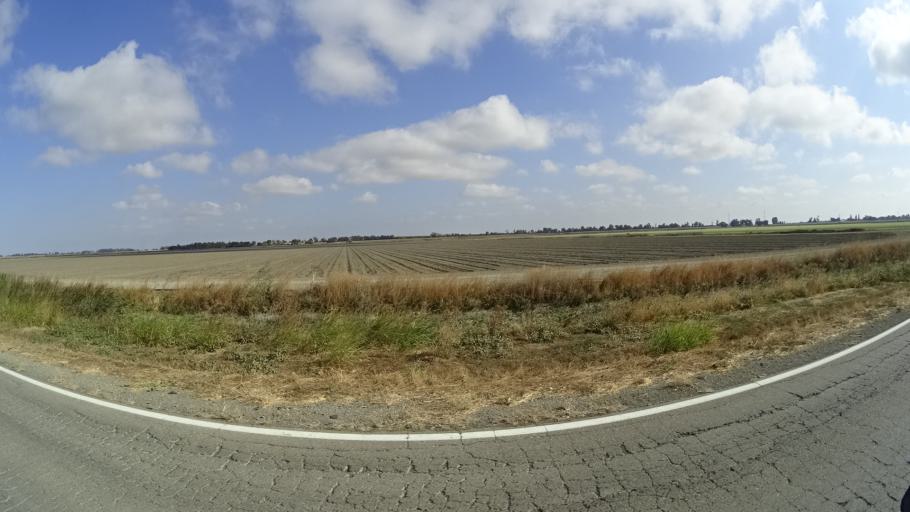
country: US
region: California
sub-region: Yolo County
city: Woodland
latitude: 38.8224
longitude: -121.7439
